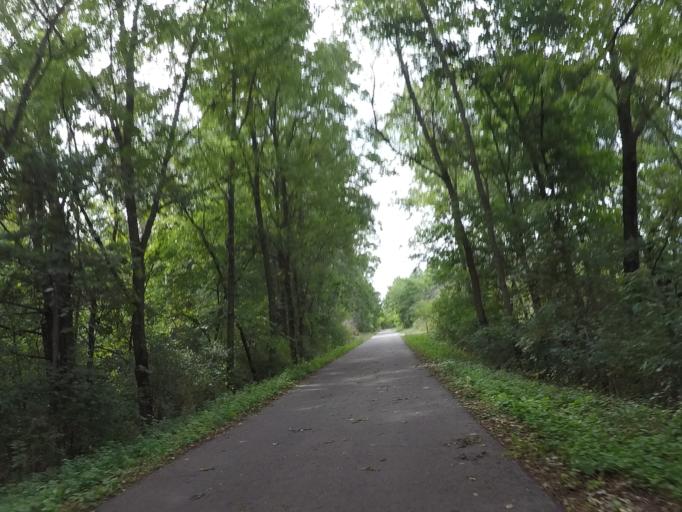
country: US
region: Wisconsin
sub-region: Sauk County
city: Prairie du Sac
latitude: 43.3079
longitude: -89.7317
